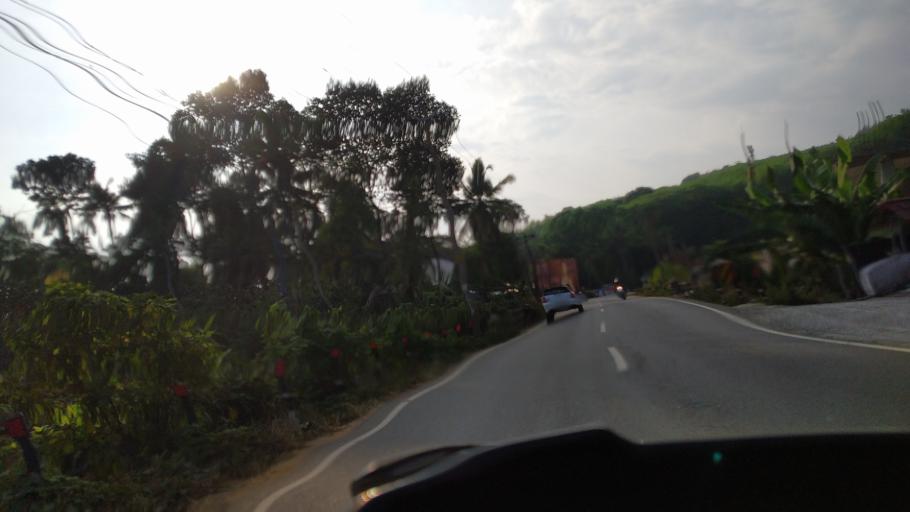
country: IN
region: Kerala
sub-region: Kottayam
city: Erattupetta
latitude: 9.5705
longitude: 76.8213
